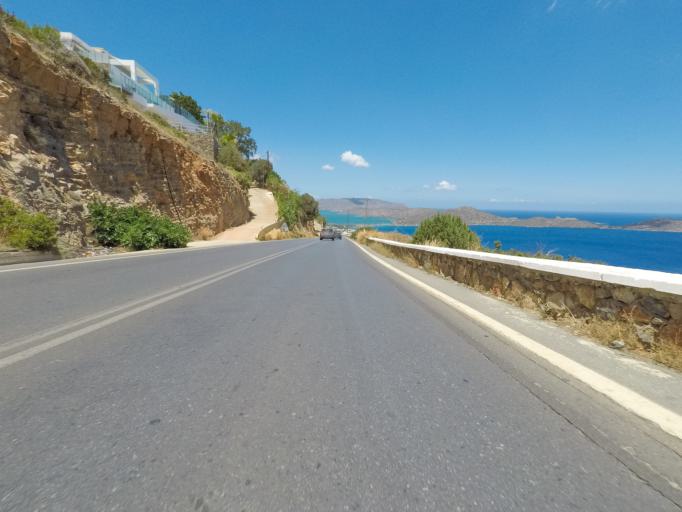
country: GR
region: Crete
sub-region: Nomos Lasithiou
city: Skhisma
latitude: 35.2351
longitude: 25.7282
